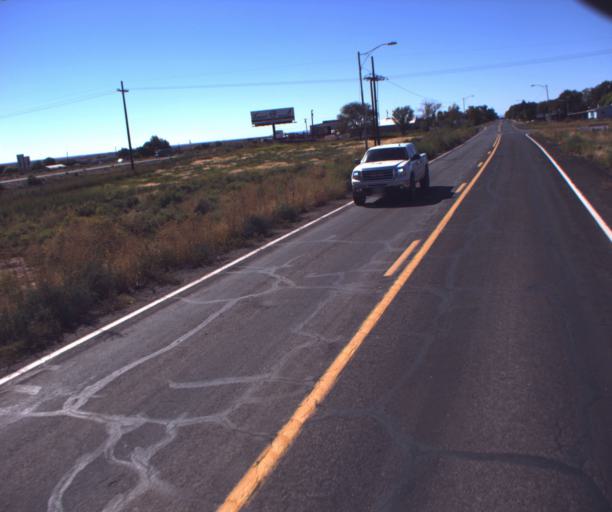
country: US
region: Arizona
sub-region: Navajo County
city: Joseph City
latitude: 34.9560
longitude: -110.3226
